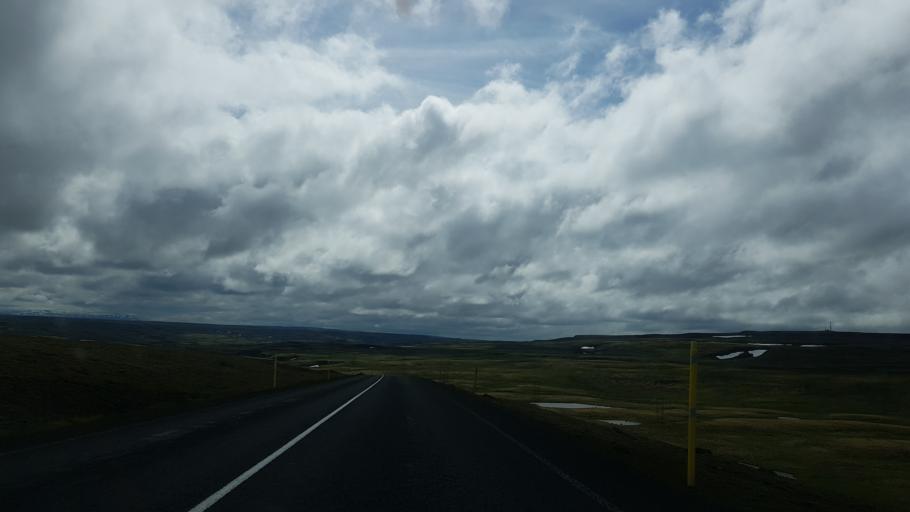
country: IS
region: West
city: Borgarnes
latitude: 64.9762
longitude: -21.0661
